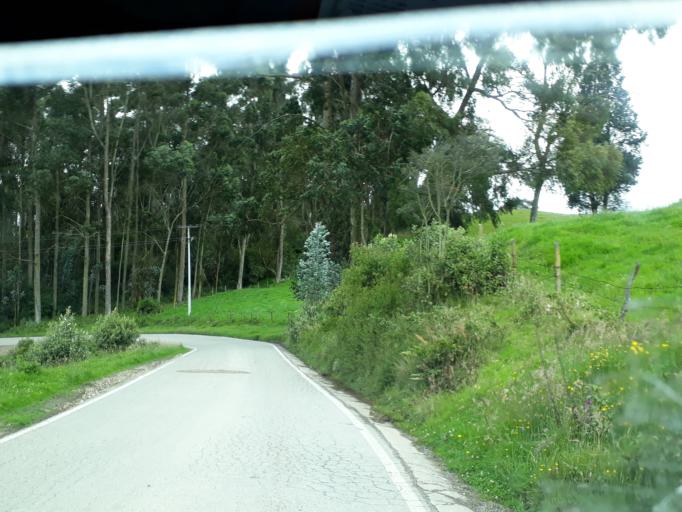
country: CO
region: Cundinamarca
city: Sutatausa
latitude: 5.1966
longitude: -73.8996
